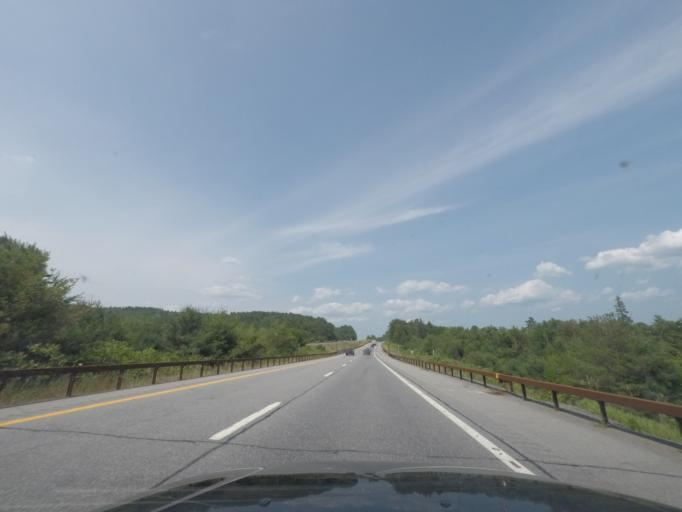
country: US
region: New York
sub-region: Warren County
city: Warrensburg
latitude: 43.7792
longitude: -73.7989
